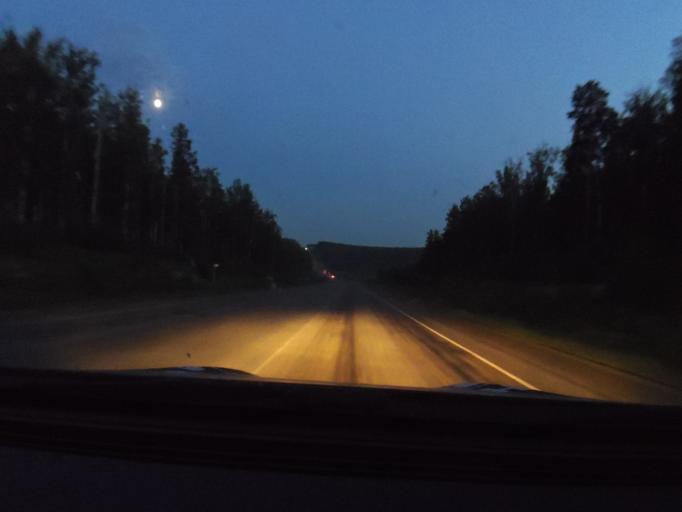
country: RU
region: Bashkortostan
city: Duvan
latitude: 55.9733
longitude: 58.2057
